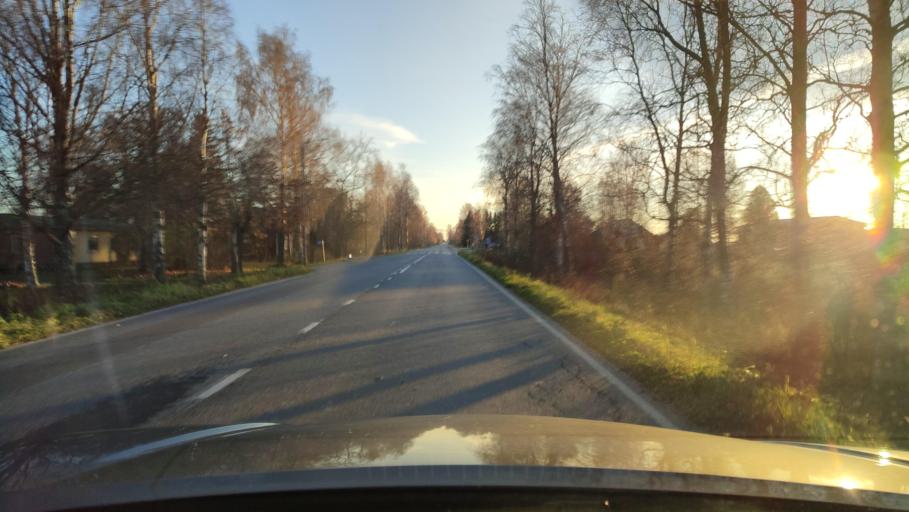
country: FI
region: Ostrobothnia
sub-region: Sydosterbotten
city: Naerpes
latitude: 62.5510
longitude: 21.4028
